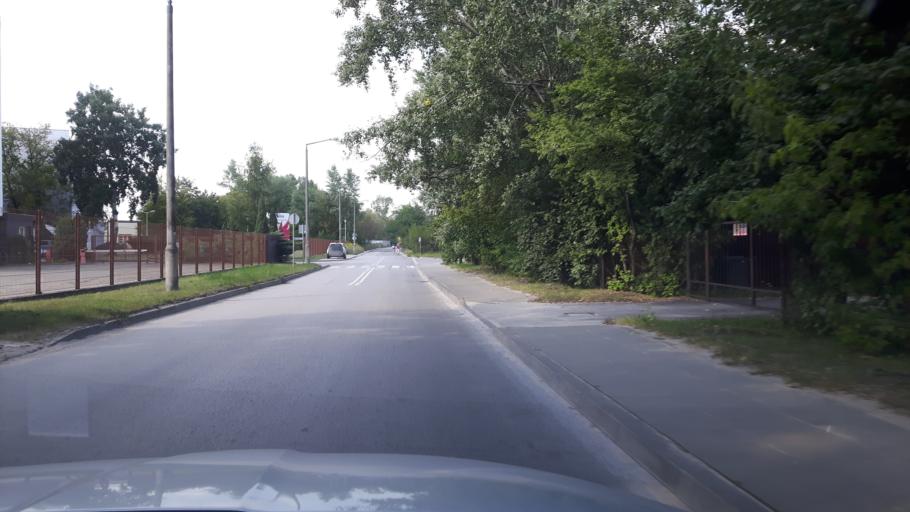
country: PL
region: Masovian Voivodeship
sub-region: Warszawa
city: Praga Polnoc
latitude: 52.2667
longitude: 21.0228
